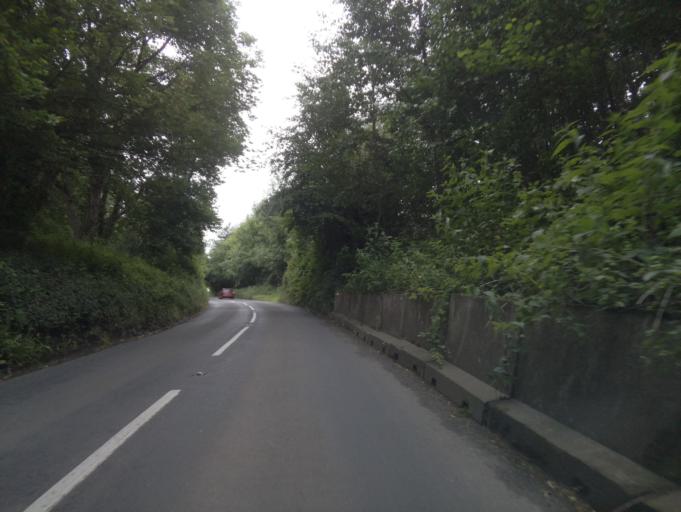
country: GB
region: England
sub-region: Devon
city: Chudleigh
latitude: 50.6179
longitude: -3.6294
